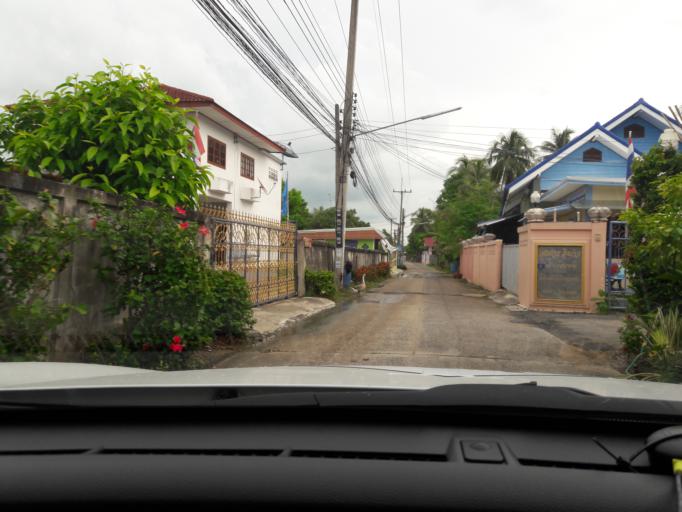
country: TH
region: Nakhon Sawan
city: Tak Fa
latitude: 15.3488
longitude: 100.5006
